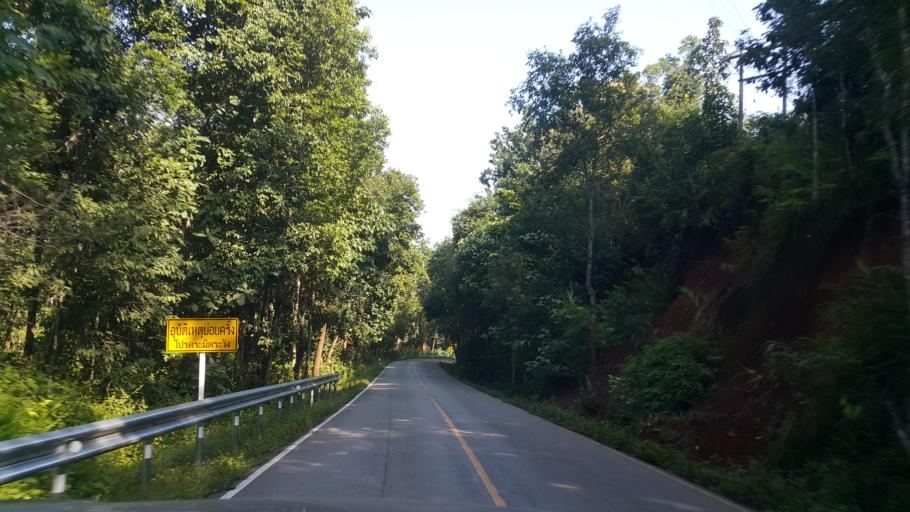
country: TH
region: Chiang Mai
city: Samoeng
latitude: 18.8588
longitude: 98.6718
